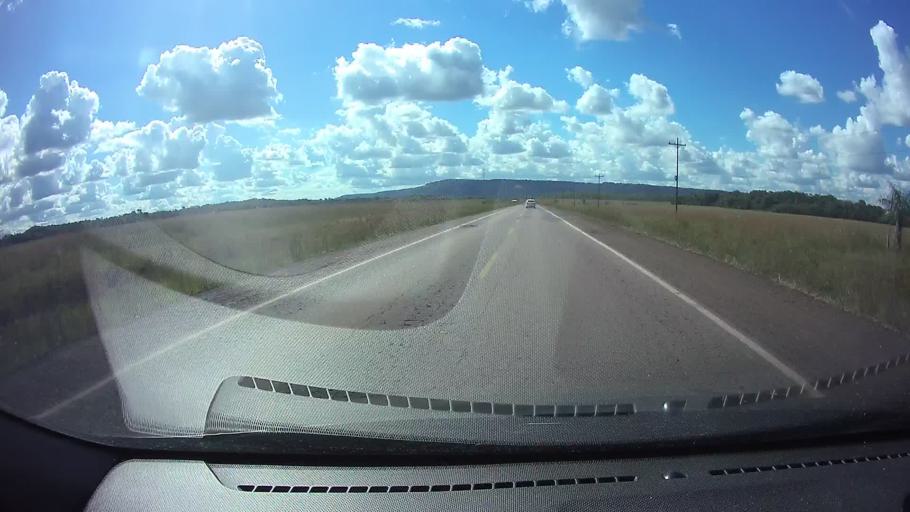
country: PY
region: Paraguari
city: Sapucai
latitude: -25.7075
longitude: -56.8442
